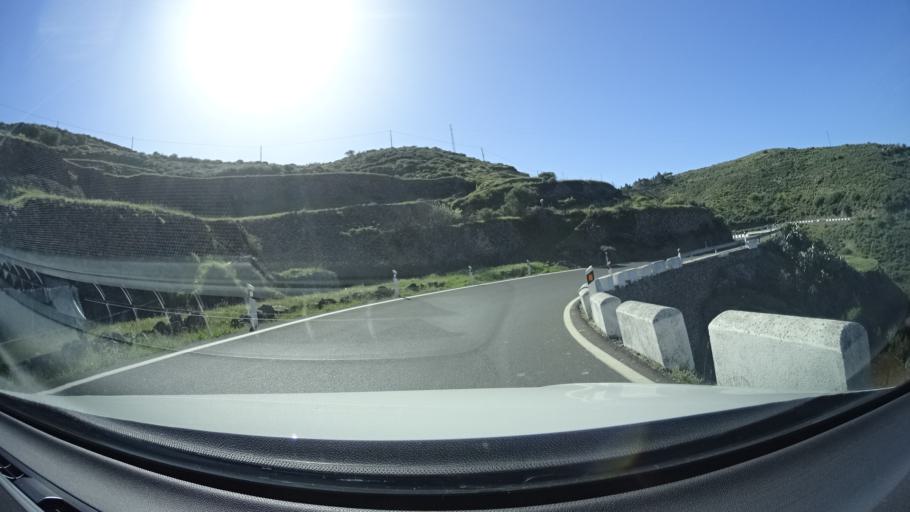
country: ES
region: Canary Islands
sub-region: Provincia de Las Palmas
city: Artenara
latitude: 28.0235
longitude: -15.6434
